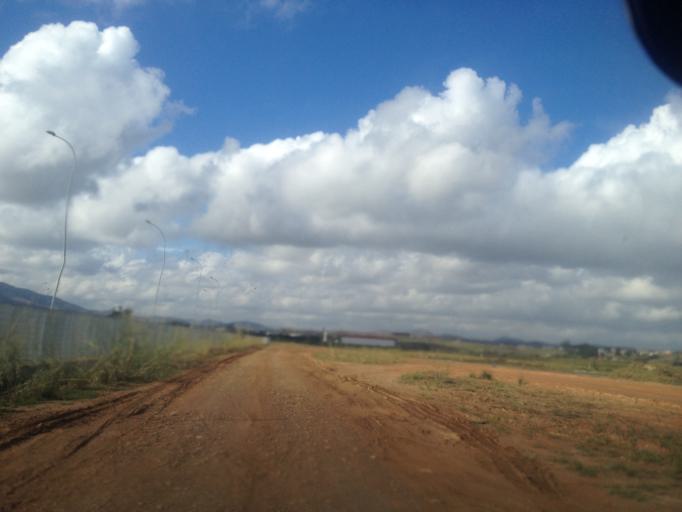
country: BR
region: Rio de Janeiro
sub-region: Resende
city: Resende
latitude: -22.4370
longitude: -44.3855
